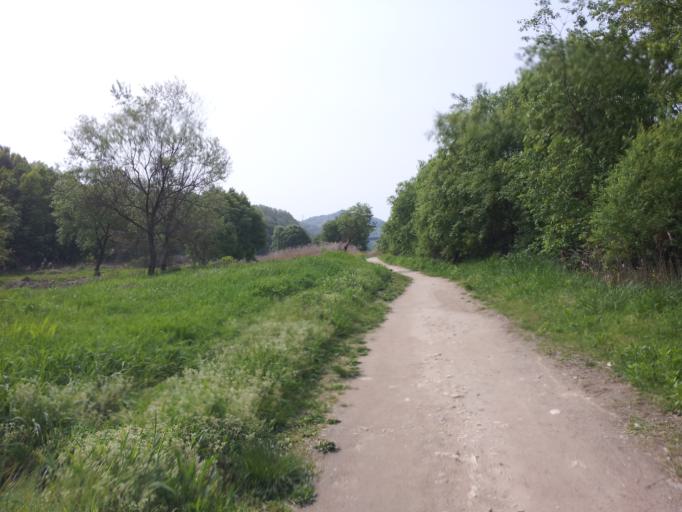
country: KR
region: Daejeon
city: Daejeon
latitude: 36.3382
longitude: 127.3539
